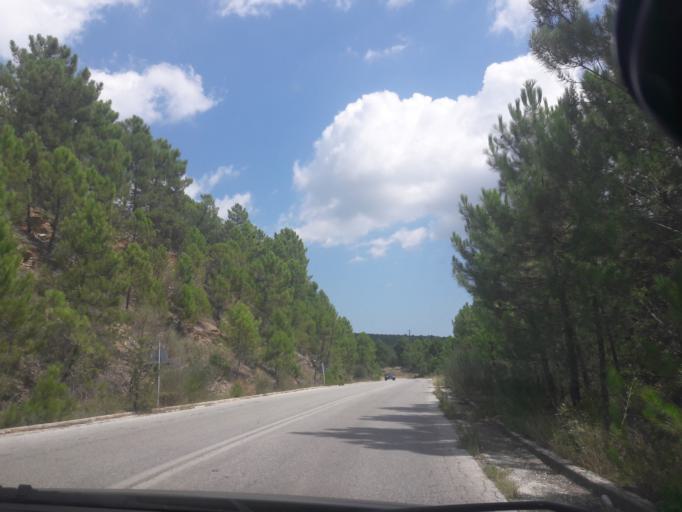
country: GR
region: Central Macedonia
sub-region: Nomos Chalkidikis
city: Polygyros
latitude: 40.3693
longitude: 23.4970
